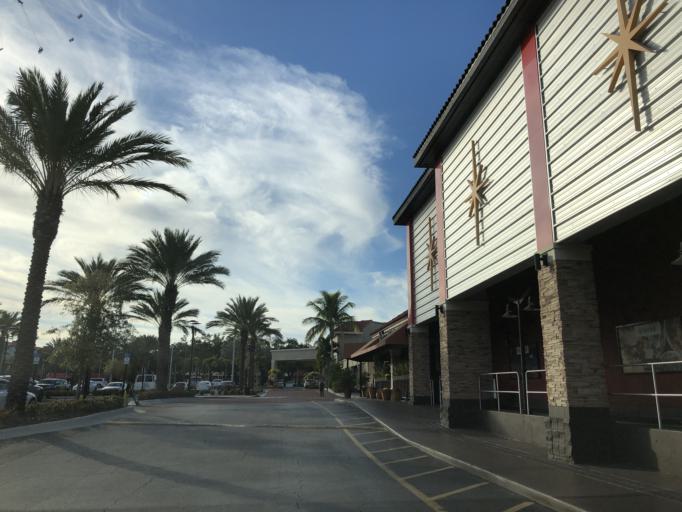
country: US
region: Florida
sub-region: Orange County
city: Doctor Phillips
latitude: 28.4454
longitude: -81.4690
